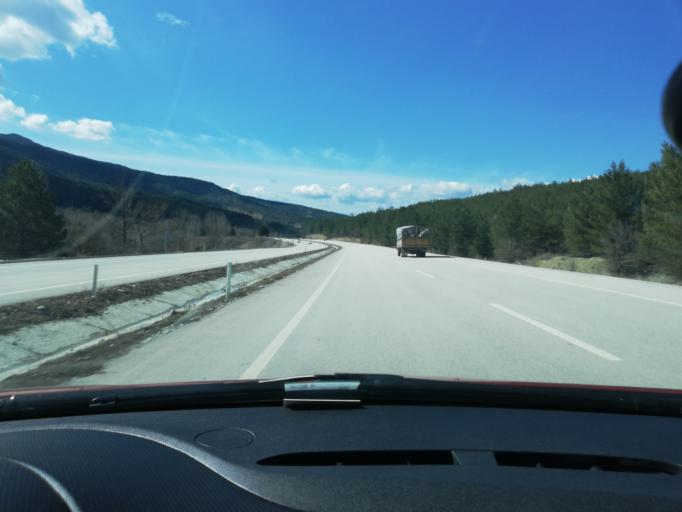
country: TR
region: Karabuk
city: Safranbolu
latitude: 41.2010
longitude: 32.8213
